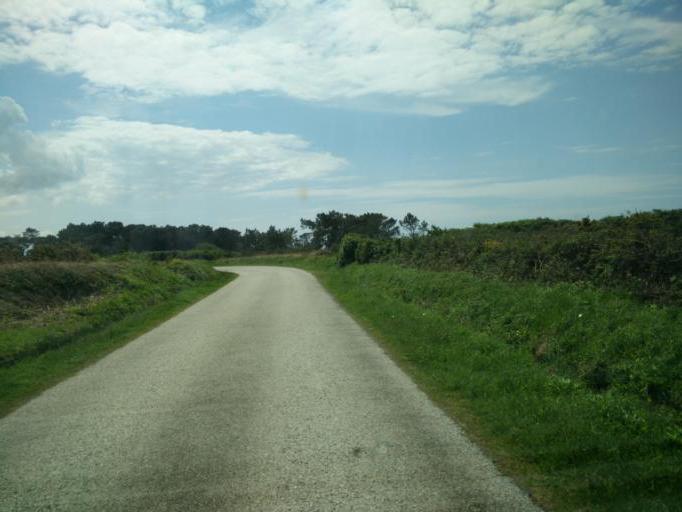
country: FR
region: Brittany
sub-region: Departement du Finistere
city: Roscanvel
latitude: 48.3226
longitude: -4.5754
